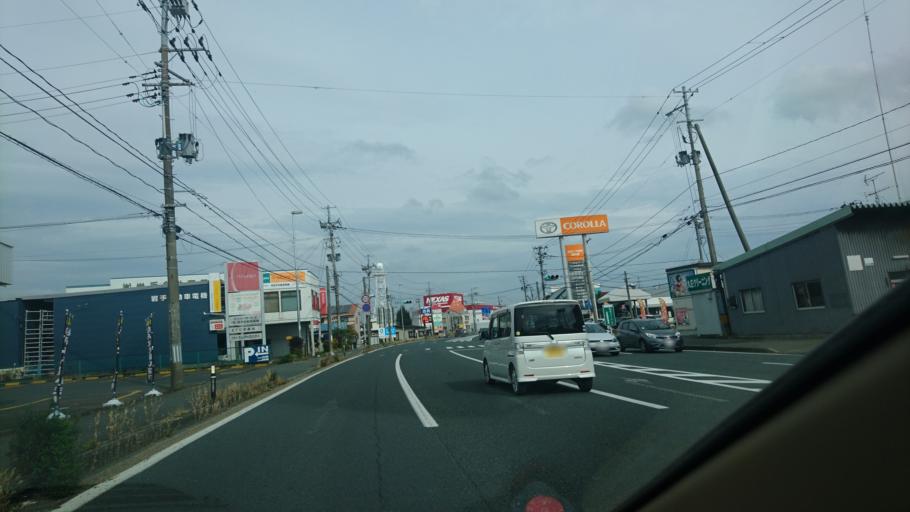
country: JP
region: Iwate
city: Morioka-shi
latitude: 39.6810
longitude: 141.1558
